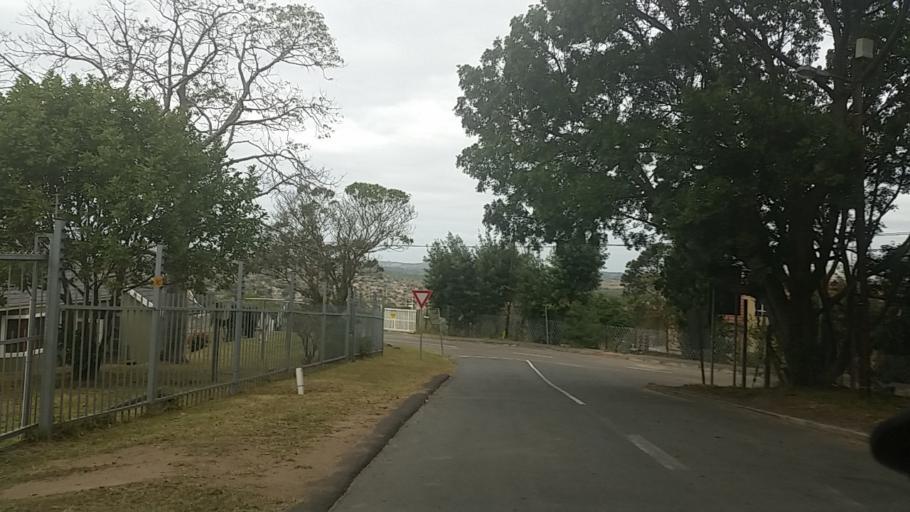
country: ZA
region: KwaZulu-Natal
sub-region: eThekwini Metropolitan Municipality
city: Berea
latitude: -29.8437
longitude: 30.9394
